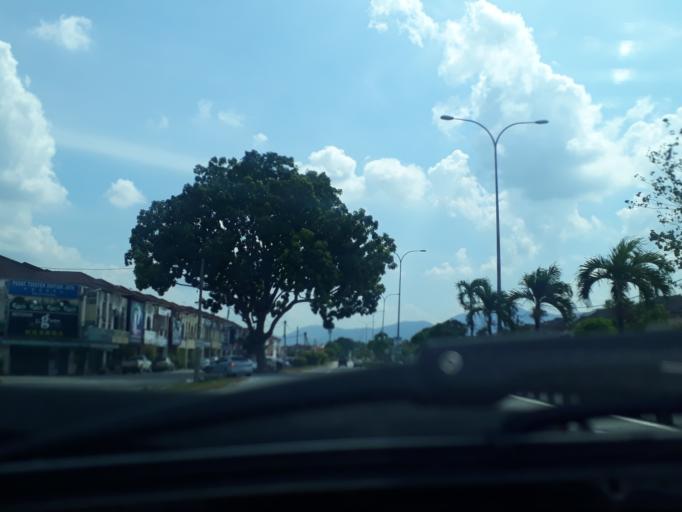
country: MY
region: Perak
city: Ipoh
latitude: 4.5774
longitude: 101.0981
